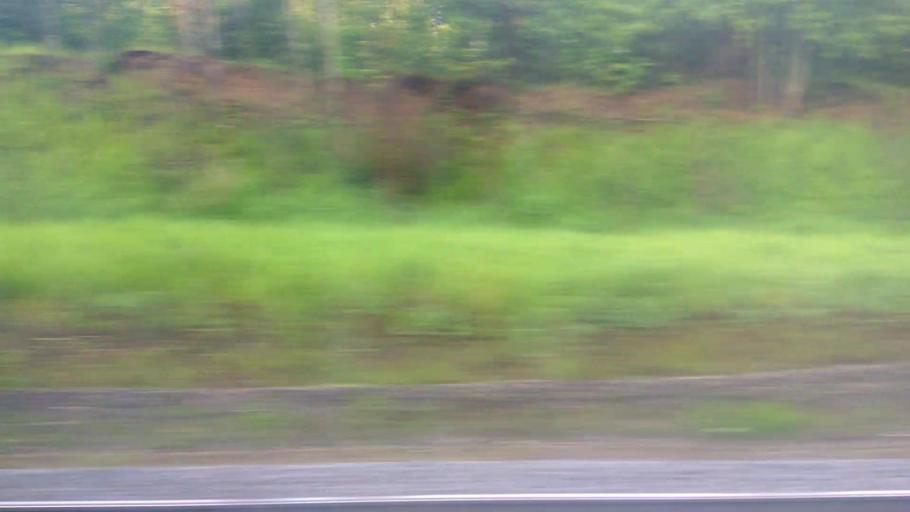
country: RU
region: Moskovskaya
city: Zhilevo
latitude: 54.9598
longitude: 38.0446
